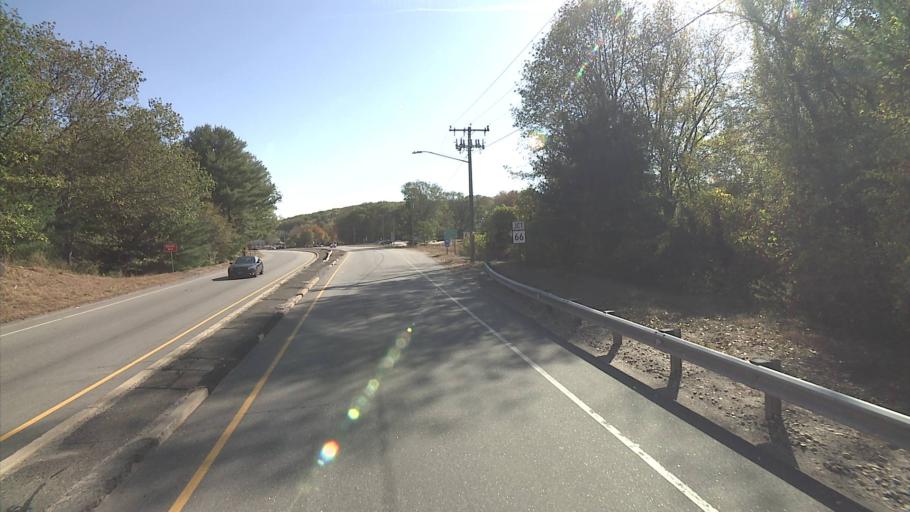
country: US
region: Connecticut
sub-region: Tolland County
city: South Coventry
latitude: 41.7199
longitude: -72.2820
